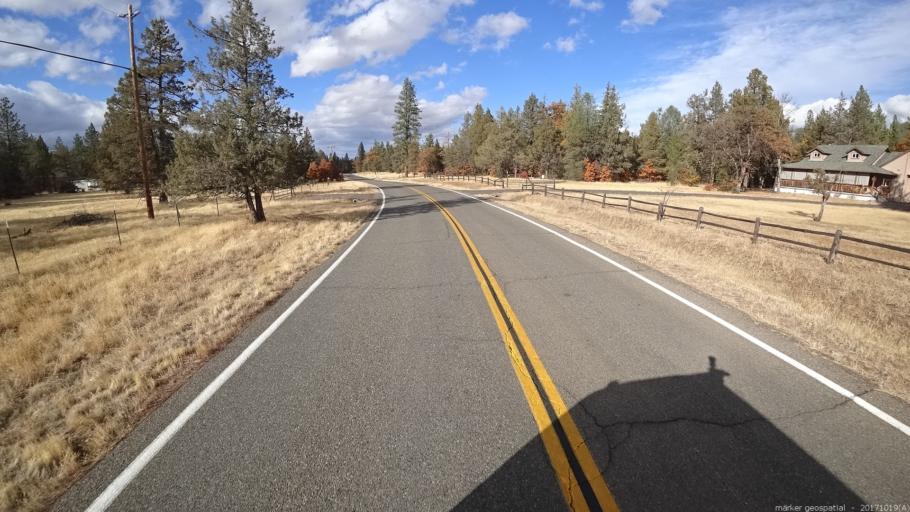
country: US
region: California
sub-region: Shasta County
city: Burney
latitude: 40.9743
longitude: -121.4329
